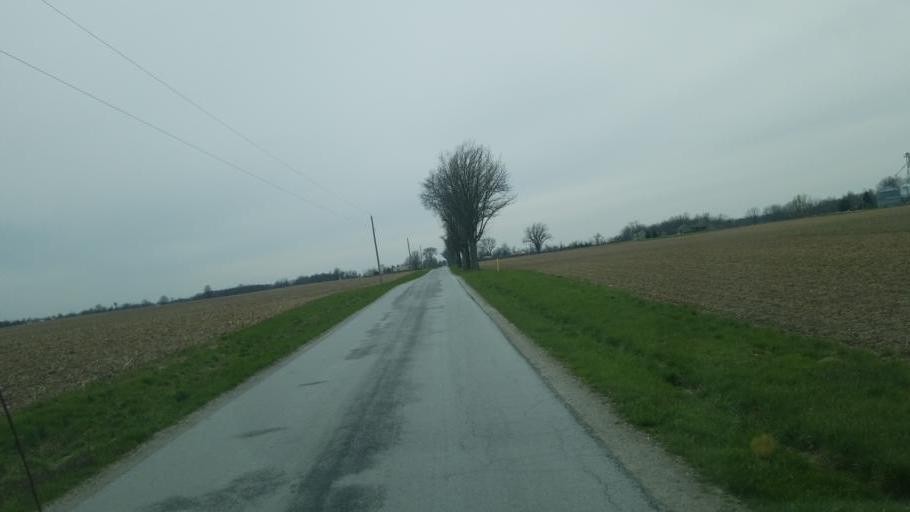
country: US
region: Ohio
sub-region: Hardin County
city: Forest
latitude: 40.8177
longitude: -83.4720
